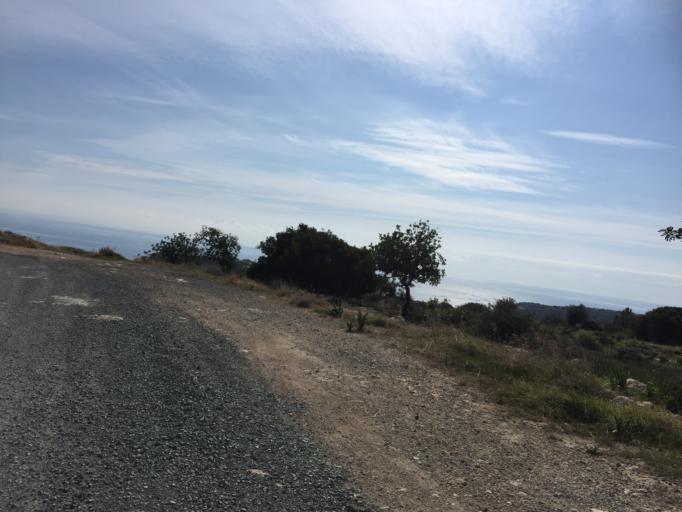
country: CY
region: Larnaka
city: Agios Tychon
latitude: 34.7410
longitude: 33.1232
